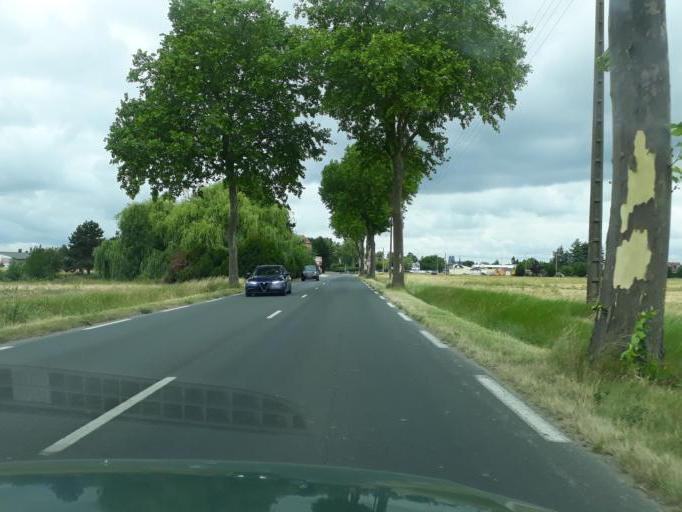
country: FR
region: Centre
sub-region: Departement du Loiret
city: Saint-Denis-en-Val
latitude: 47.8727
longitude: 1.9482
